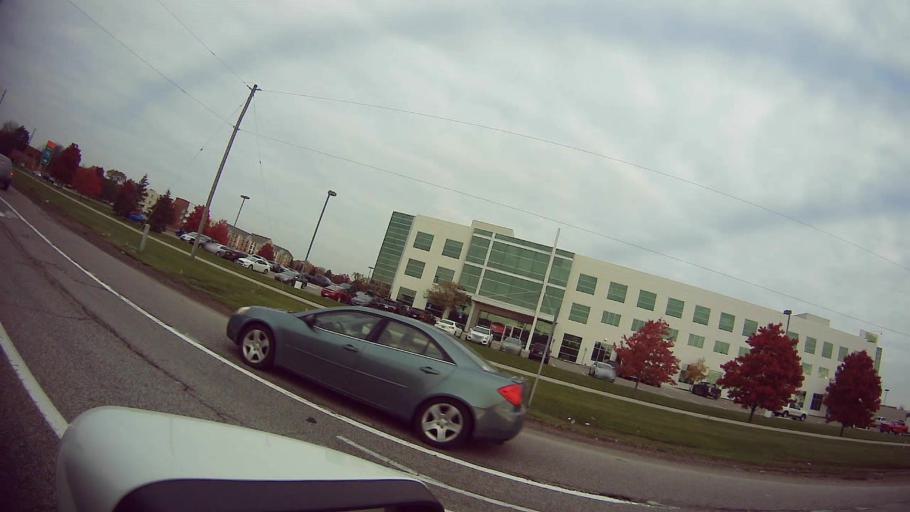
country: US
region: Michigan
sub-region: Oakland County
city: Clawson
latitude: 42.5341
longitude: -83.1187
